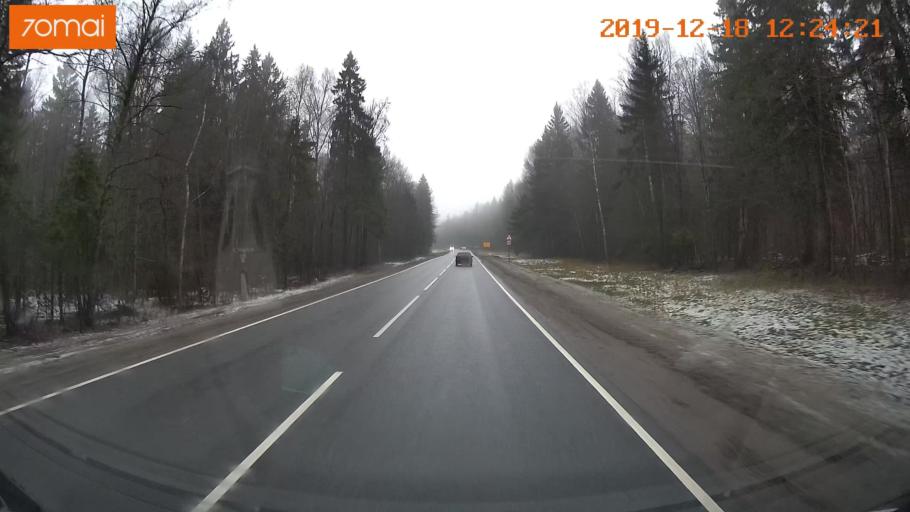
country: RU
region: Moskovskaya
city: Novopetrovskoye
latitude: 56.0235
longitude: 36.5002
